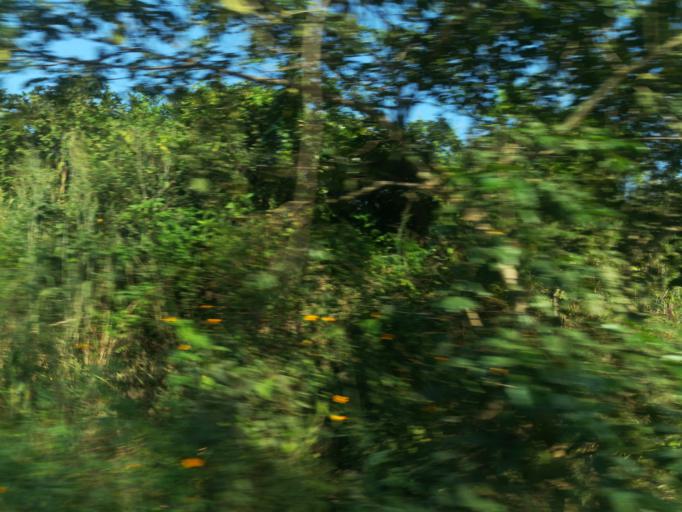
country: NG
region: Ogun
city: Abeokuta
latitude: 7.2577
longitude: 3.3003
